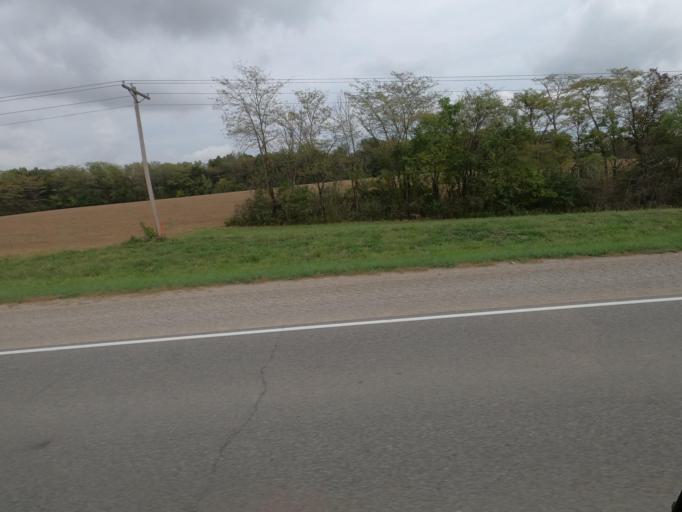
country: US
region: Iowa
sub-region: Wapello County
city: Ottumwa
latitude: 40.9403
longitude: -92.2271
